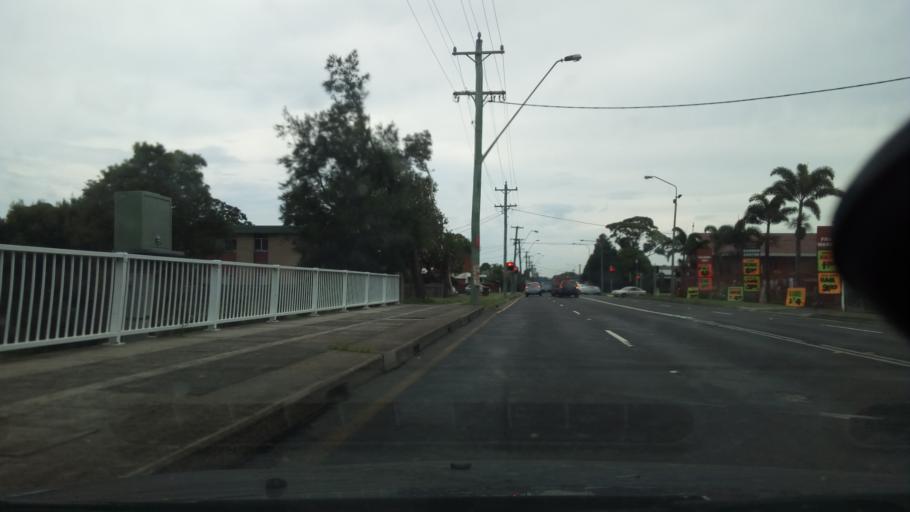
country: AU
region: New South Wales
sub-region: Wollongong
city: Fairy Meadow
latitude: -34.3967
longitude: 150.8925
